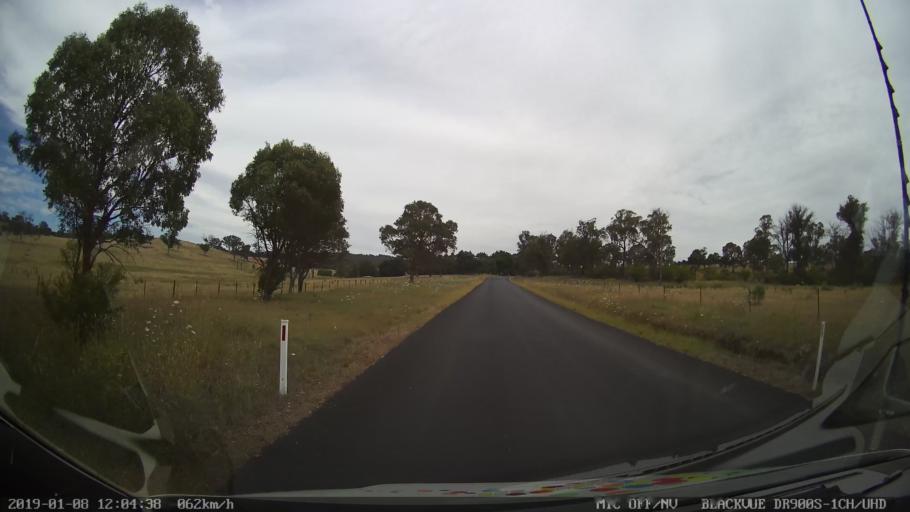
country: AU
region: New South Wales
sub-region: Armidale Dumaresq
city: Armidale
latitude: -30.4414
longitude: 151.5899
